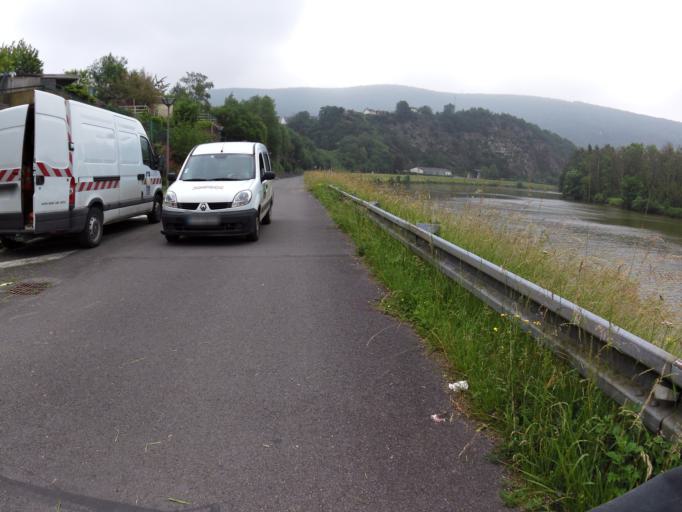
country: FR
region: Champagne-Ardenne
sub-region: Departement des Ardennes
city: Fumay
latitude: 49.9895
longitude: 4.6999
